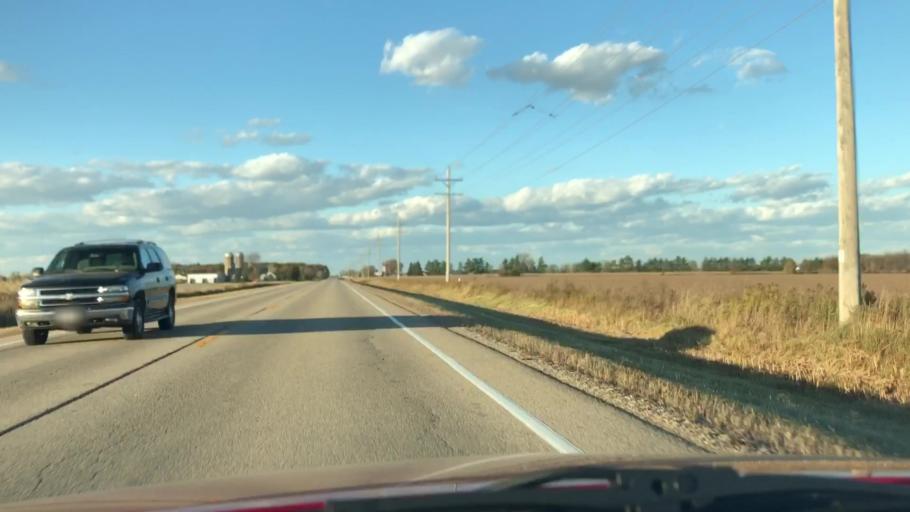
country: US
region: Wisconsin
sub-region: Outagamie County
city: Seymour
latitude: 44.4783
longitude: -88.2911
